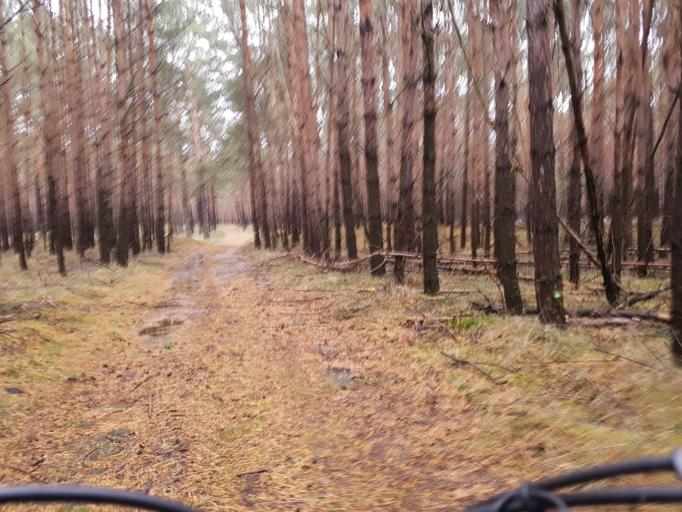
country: DE
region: Brandenburg
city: Schilda
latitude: 51.6195
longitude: 13.3837
